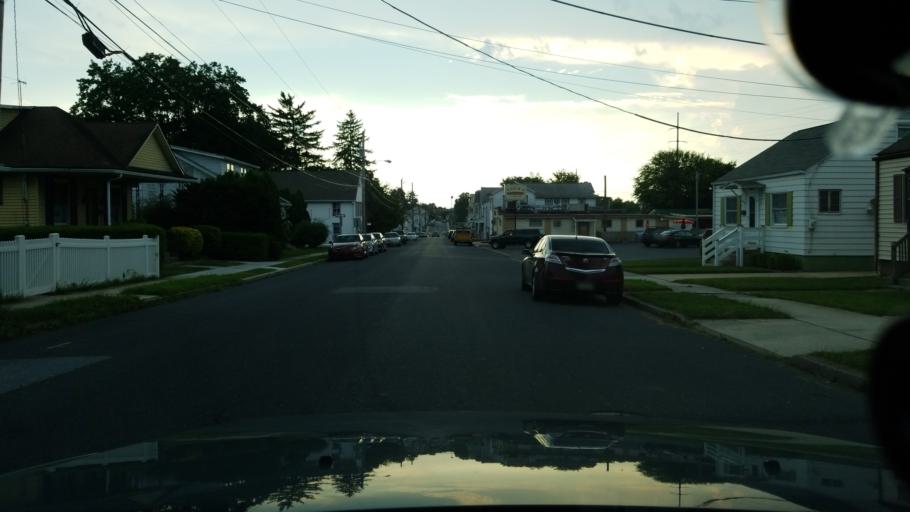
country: US
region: Pennsylvania
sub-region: Dauphin County
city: Hummelstown
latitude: 40.2668
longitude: -76.7041
